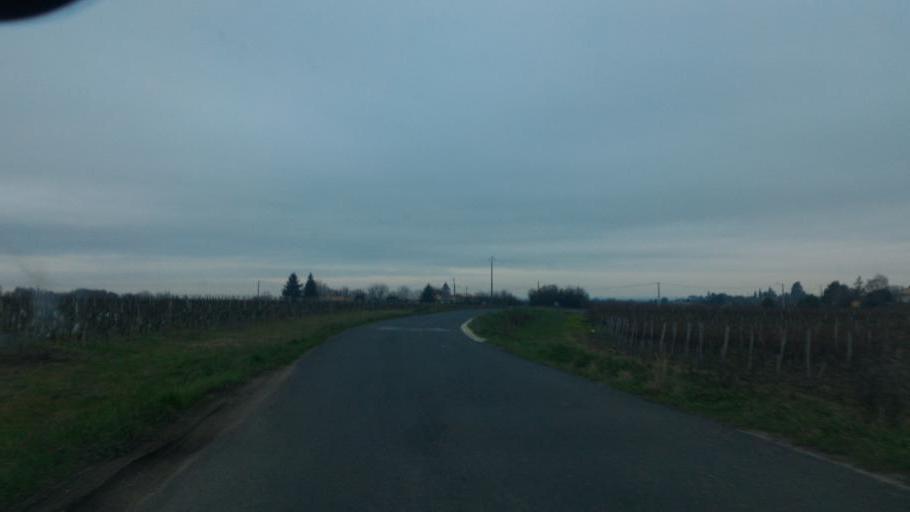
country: FR
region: Aquitaine
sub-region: Departement de la Gironde
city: Saint-Martin-Lacaussade
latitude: 45.1432
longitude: -0.6312
